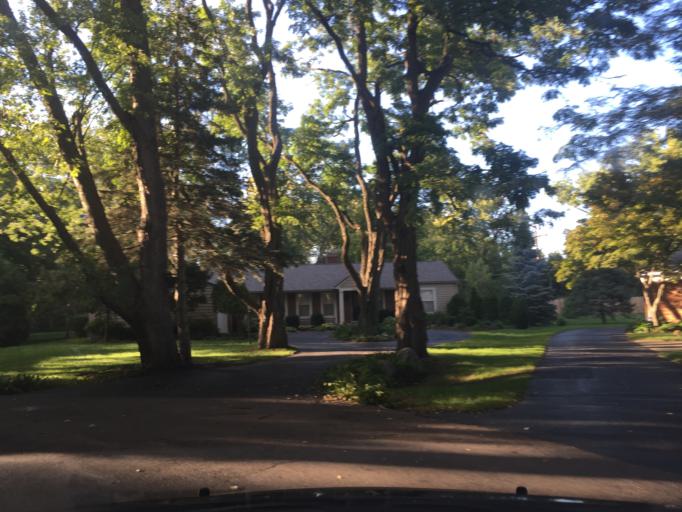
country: US
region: Michigan
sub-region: Oakland County
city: Franklin
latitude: 42.5578
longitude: -83.2892
